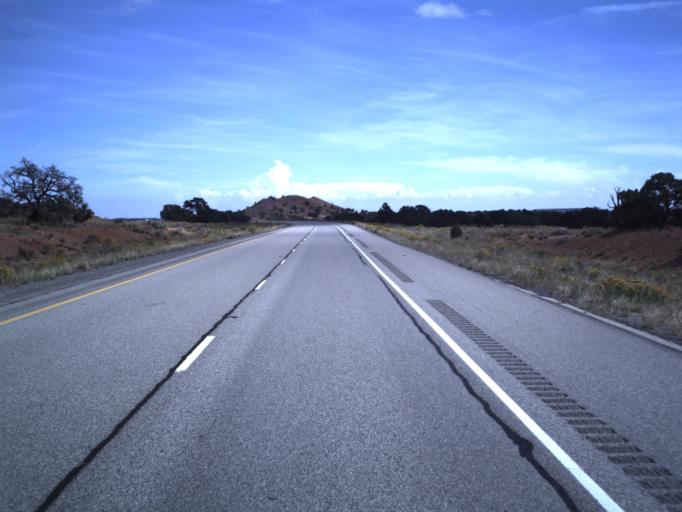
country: US
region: Utah
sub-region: Emery County
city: Castle Dale
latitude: 38.8682
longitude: -110.7186
